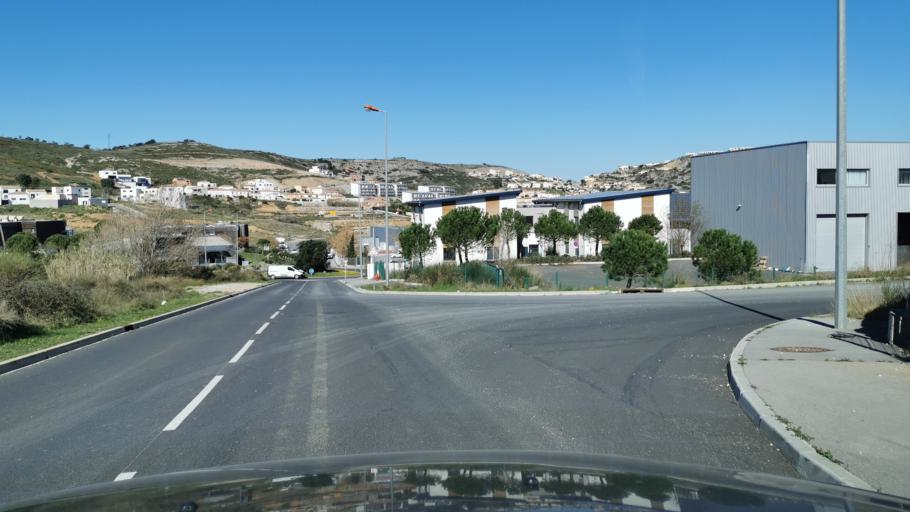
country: FR
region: Languedoc-Roussillon
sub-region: Departement de l'Aude
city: Narbonne
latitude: 43.1547
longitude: 2.9676
